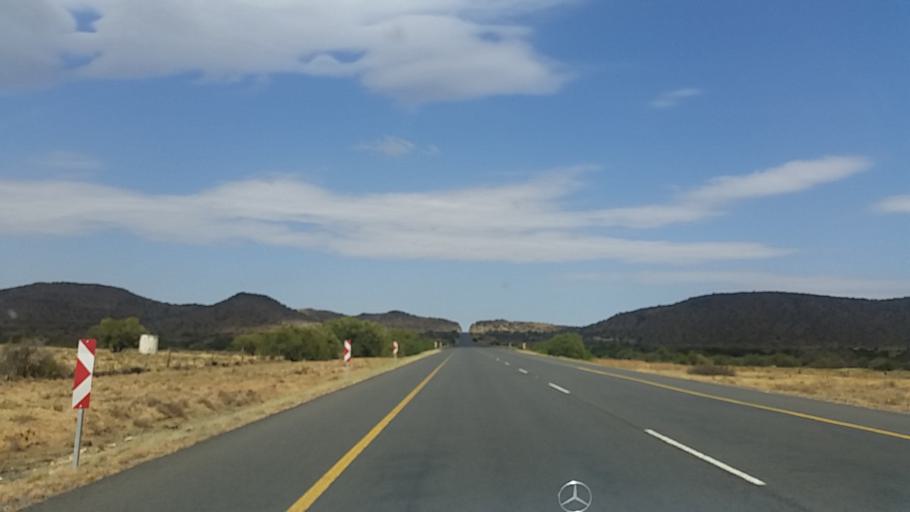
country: ZA
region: Northern Cape
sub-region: Pixley ka Seme District Municipality
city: Colesberg
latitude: -30.6372
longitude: 25.2344
